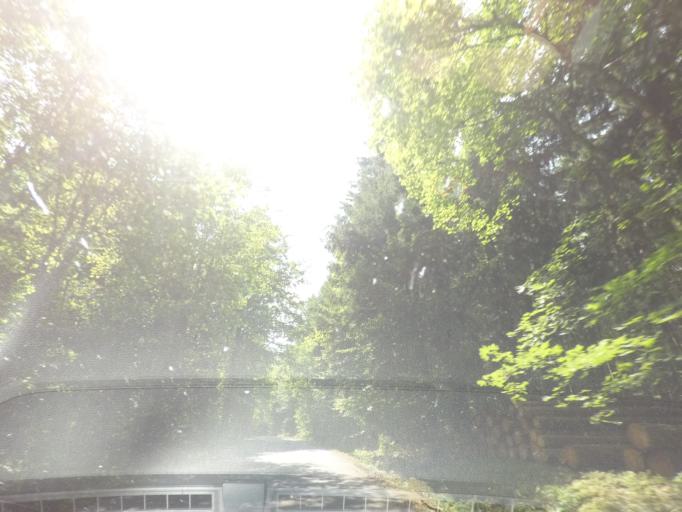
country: CZ
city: Radvanice
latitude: 50.6107
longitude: 16.0596
